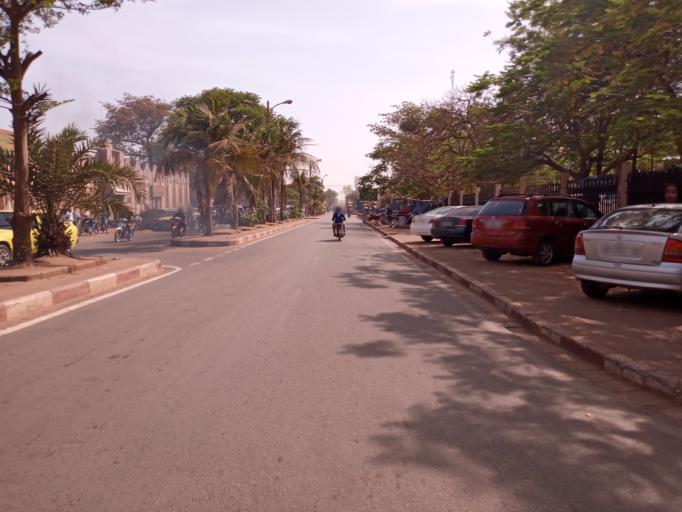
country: ML
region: Bamako
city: Bamako
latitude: 12.6393
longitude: -7.9939
